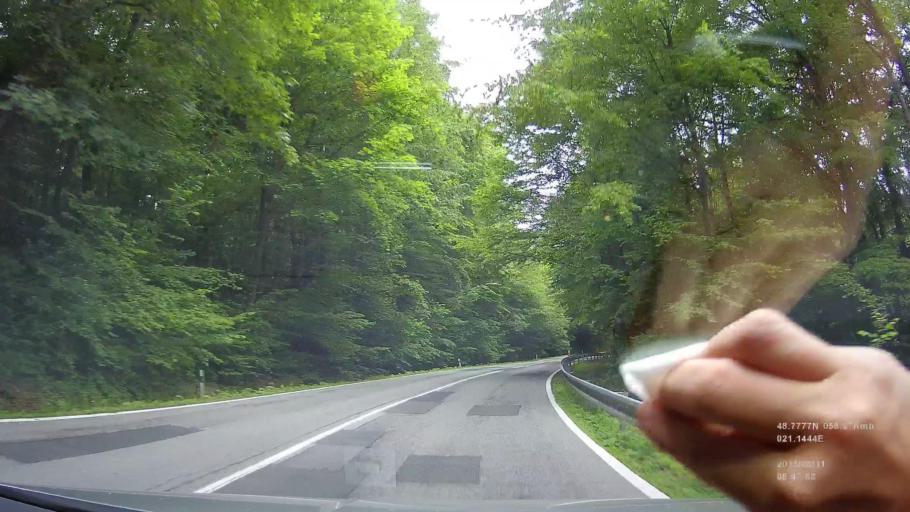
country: SK
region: Kosicky
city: Kosice
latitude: 48.7737
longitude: 21.1482
